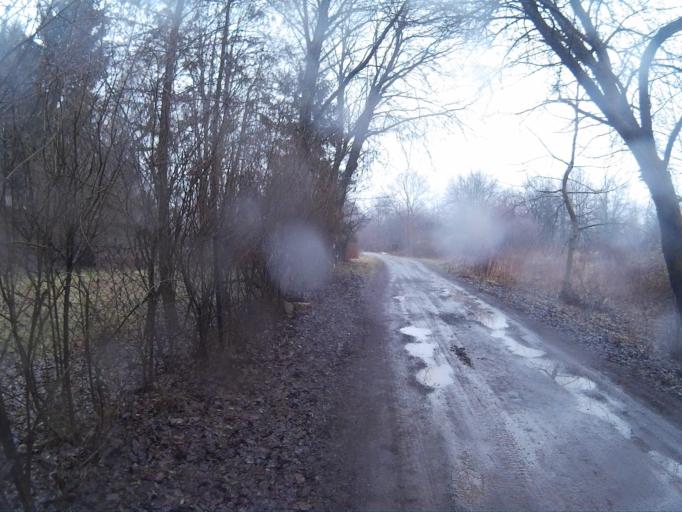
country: HU
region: Nograd
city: Somoskoujfalu
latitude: 48.1597
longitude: 19.8541
